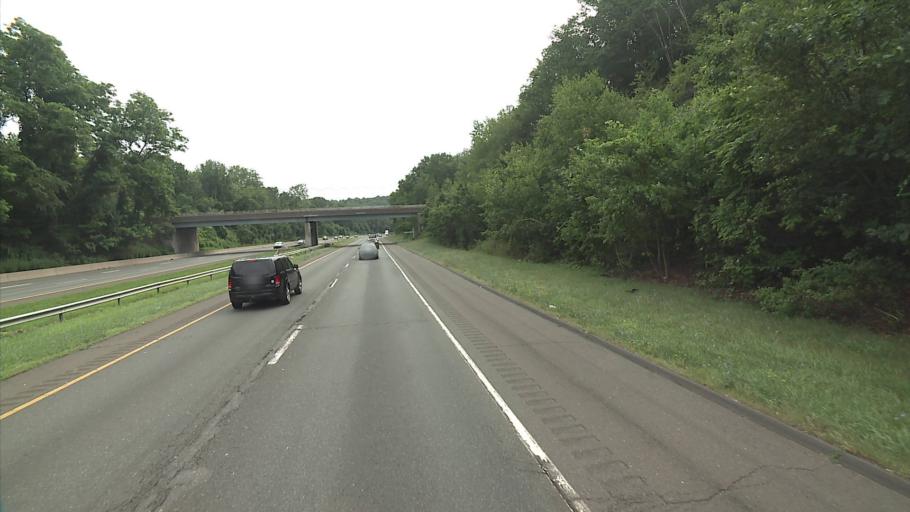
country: US
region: Connecticut
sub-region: Fairfield County
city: Newtown
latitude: 41.4276
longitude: -73.3218
